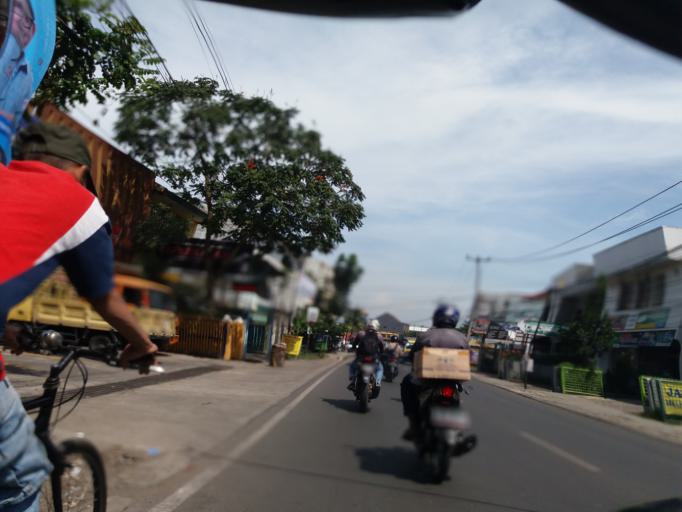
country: ID
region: West Java
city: Margahayukencana
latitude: -6.9346
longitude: 107.5714
